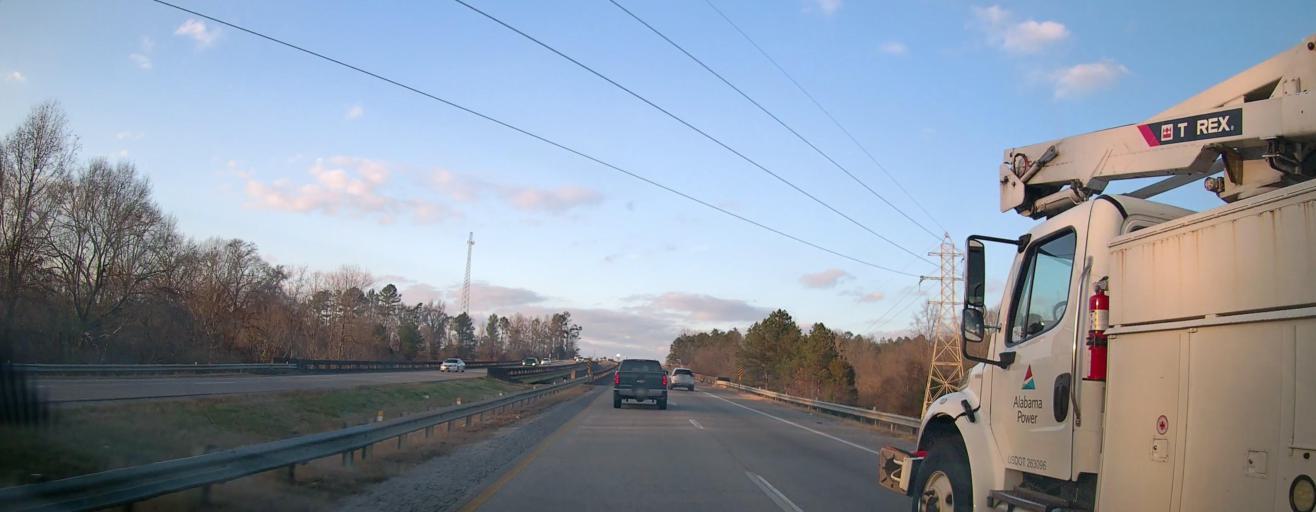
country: US
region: Alabama
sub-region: Calhoun County
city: Alexandria
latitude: 33.8161
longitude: -85.9059
